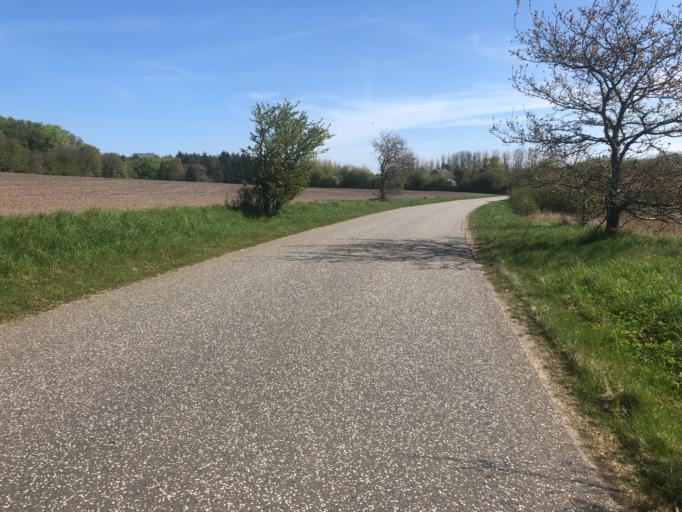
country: DK
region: Central Jutland
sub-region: Holstebro Kommune
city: Vinderup
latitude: 56.5711
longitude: 8.7844
